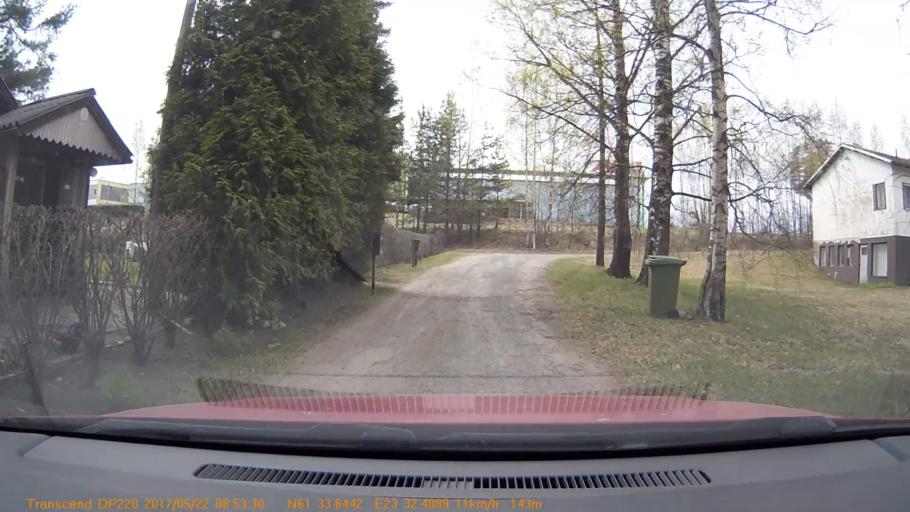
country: FI
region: Pirkanmaa
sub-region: Tampere
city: Yloejaervi
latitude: 61.5608
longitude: 23.5402
